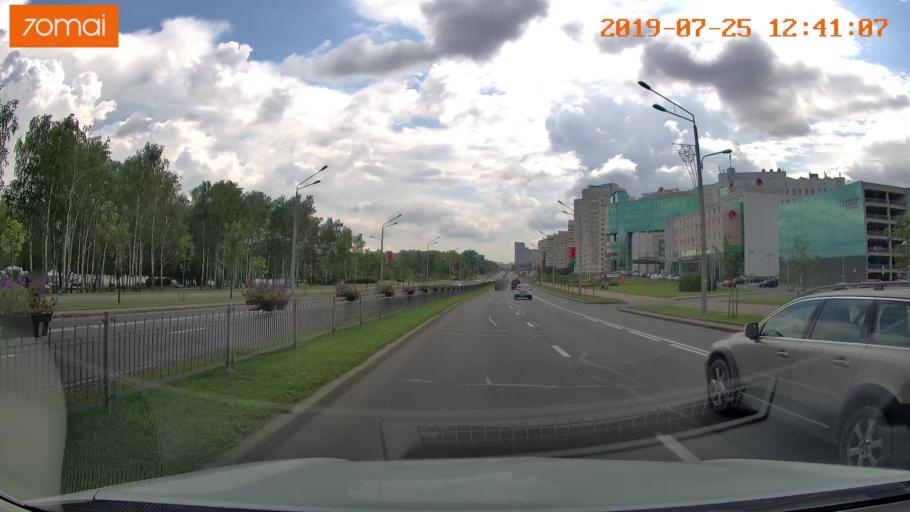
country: BY
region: Minsk
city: Minsk
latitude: 53.9231
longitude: 27.5263
